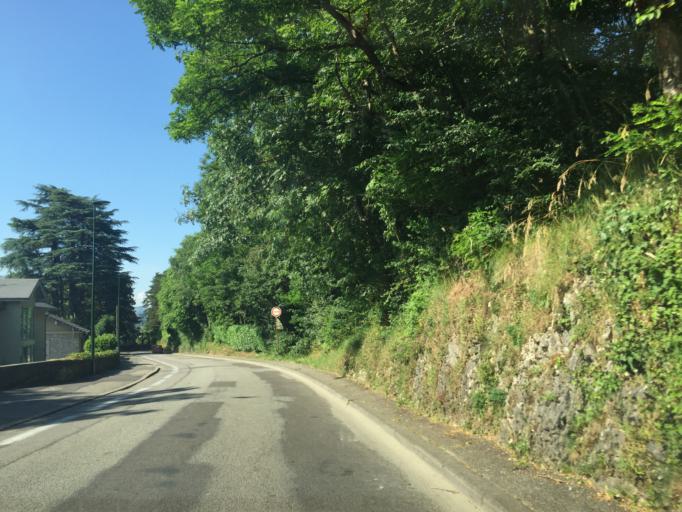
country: FR
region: Rhone-Alpes
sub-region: Departement de la Savoie
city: Tresserve
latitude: 45.6787
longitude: 5.9124
